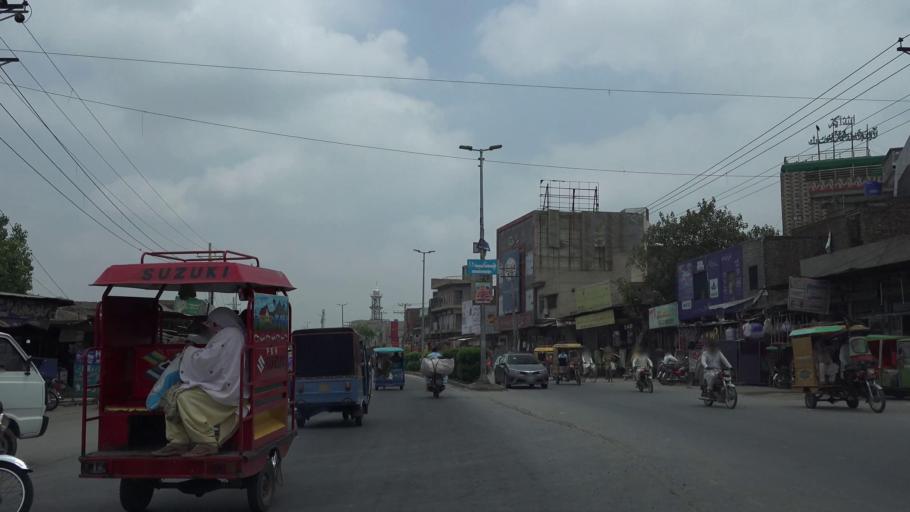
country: PK
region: Punjab
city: Faisalabad
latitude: 31.4052
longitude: 73.1242
